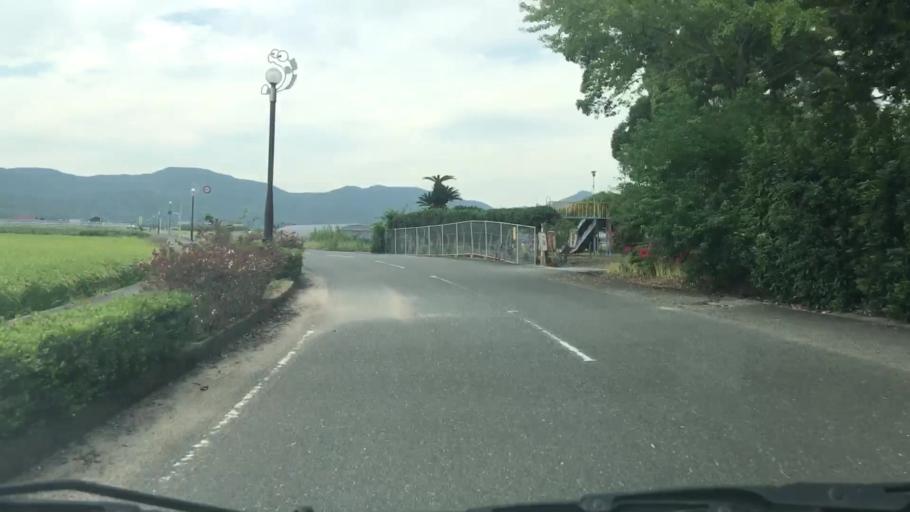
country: JP
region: Saga Prefecture
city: Kashima
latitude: 33.1455
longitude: 130.1431
